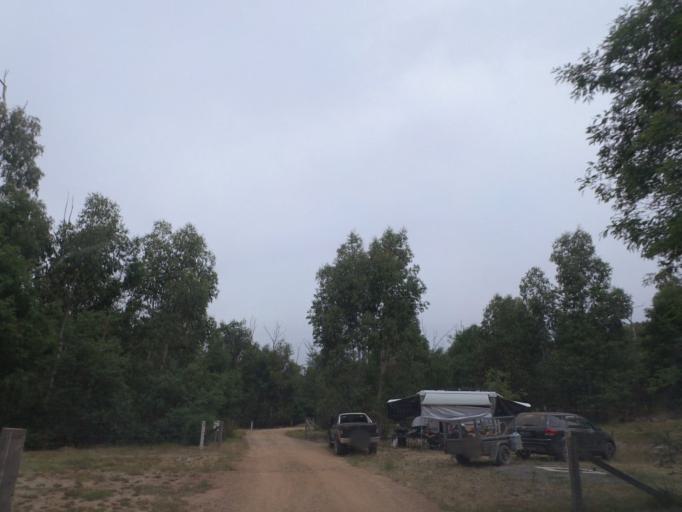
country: AU
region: Victoria
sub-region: Yarra Ranges
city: Healesville
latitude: -37.4262
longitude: 145.5695
